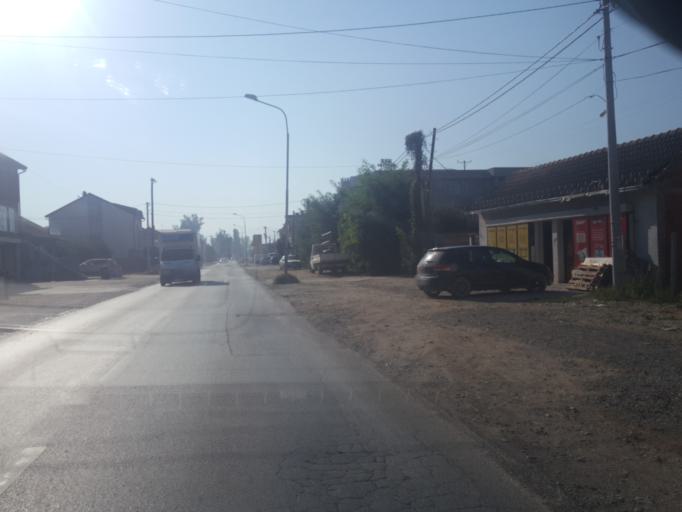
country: XK
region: Gjakova
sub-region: Komuna e Gjakoves
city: Gjakove
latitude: 42.4011
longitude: 20.4150
